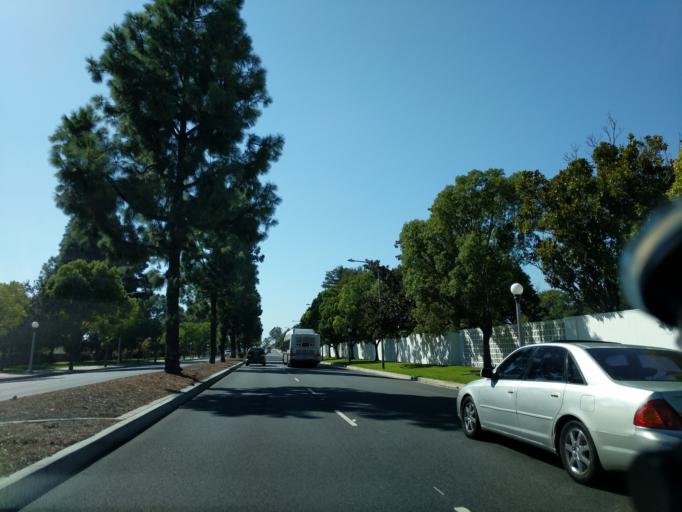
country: US
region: California
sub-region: Los Angeles County
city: Hawaiian Gardens
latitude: 33.8317
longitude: -118.0580
